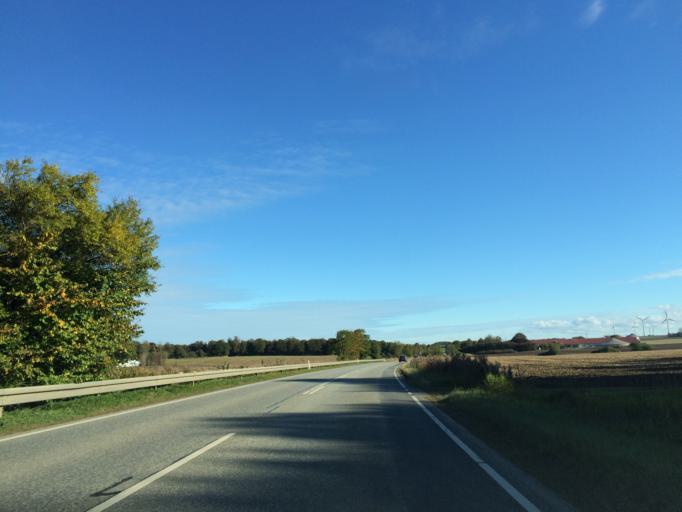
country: DK
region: Central Jutland
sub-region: Randers Kommune
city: Langa
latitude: 56.3935
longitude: 9.9737
